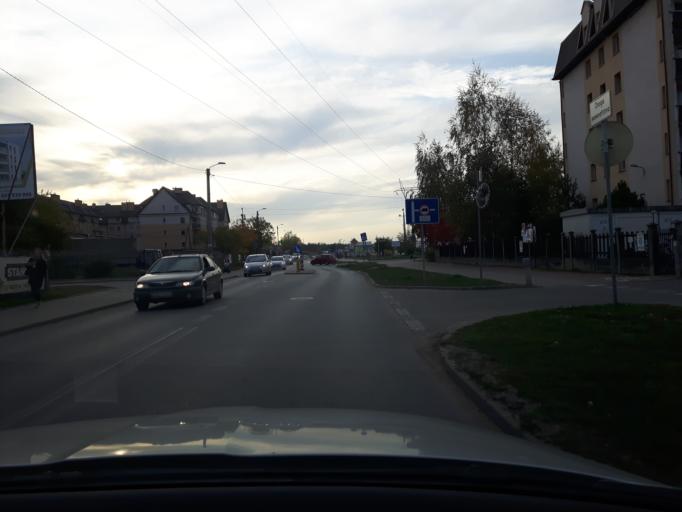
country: PL
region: Masovian Voivodeship
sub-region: Powiat wolominski
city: Zabki
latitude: 52.2786
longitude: 21.1201
